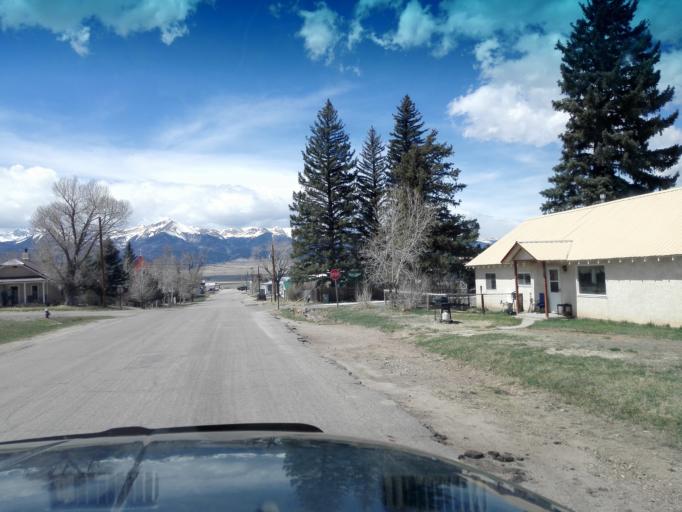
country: US
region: Colorado
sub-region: Custer County
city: Westcliffe
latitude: 38.1349
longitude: -105.4656
